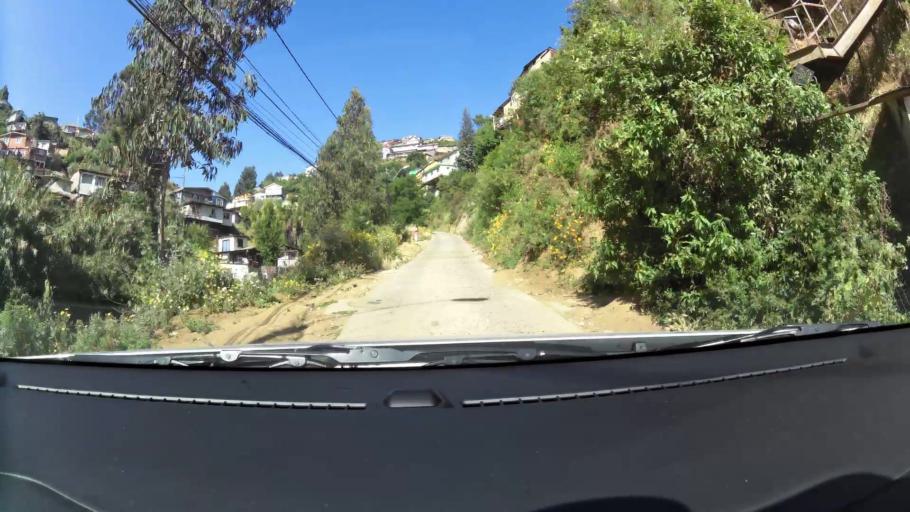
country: CL
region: Valparaiso
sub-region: Provincia de Valparaiso
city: Valparaiso
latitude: -33.0468
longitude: -71.6372
